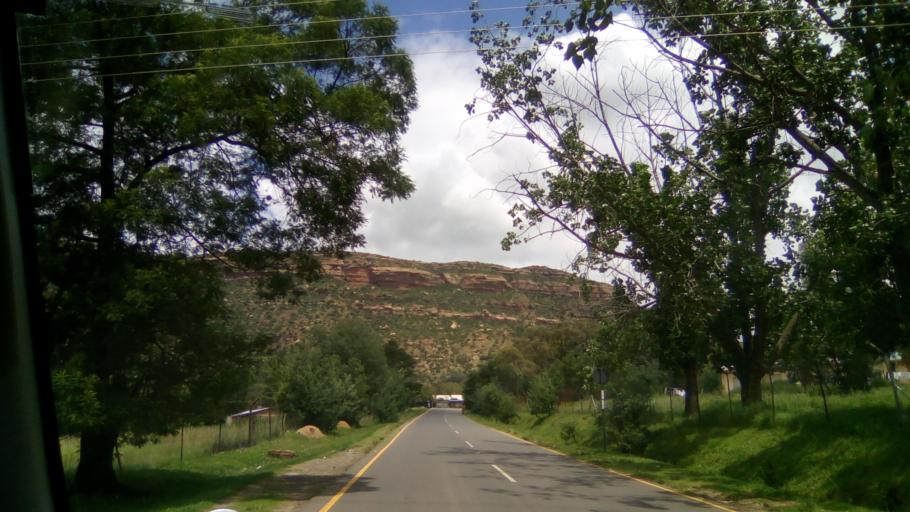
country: LS
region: Maseru
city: Nako
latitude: -29.6284
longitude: 27.5024
